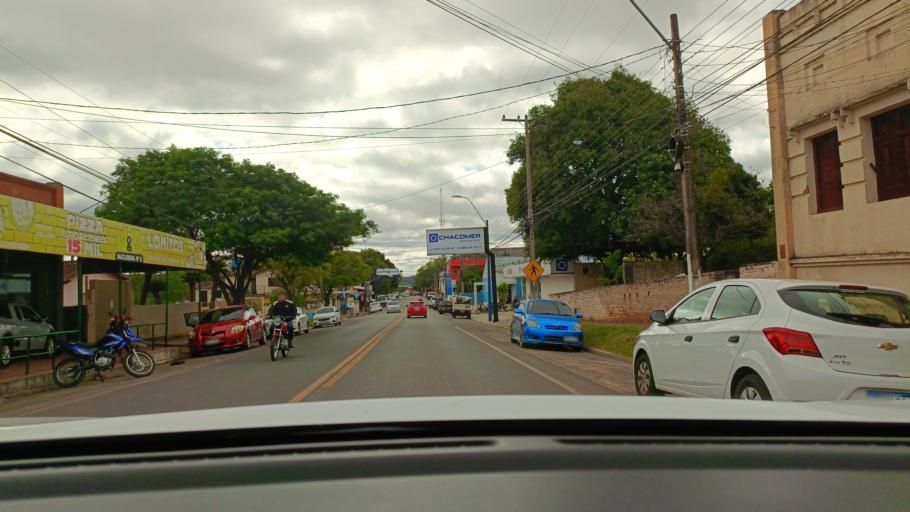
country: PY
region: San Pedro
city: Guayaybi
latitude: -24.6682
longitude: -56.4448
